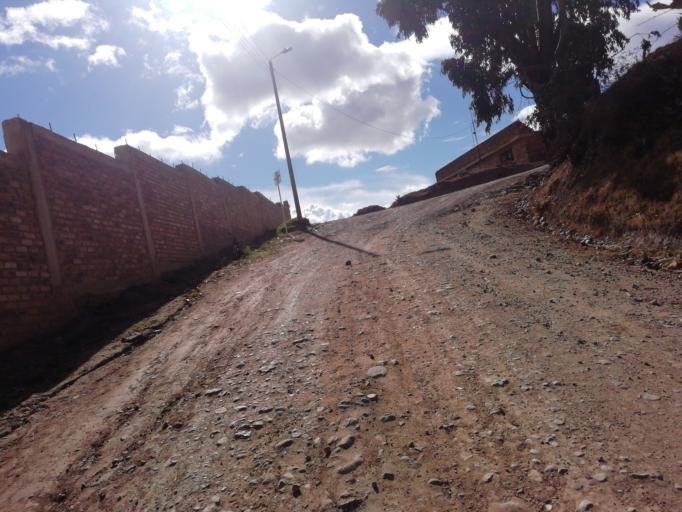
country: CO
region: Boyaca
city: Gameza
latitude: 5.8040
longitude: -72.8072
